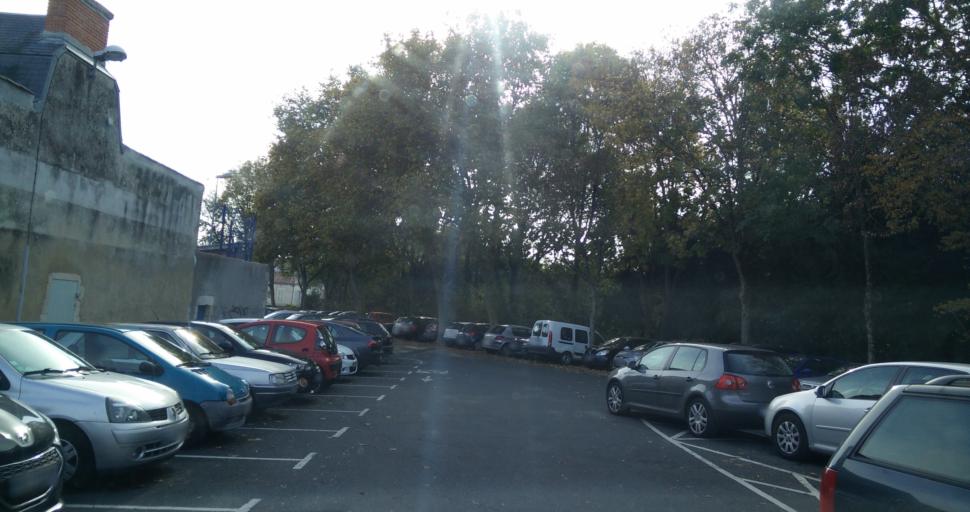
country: FR
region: Poitou-Charentes
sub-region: Departement de la Charente-Maritime
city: La Rochelle
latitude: 46.1614
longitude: -1.1564
